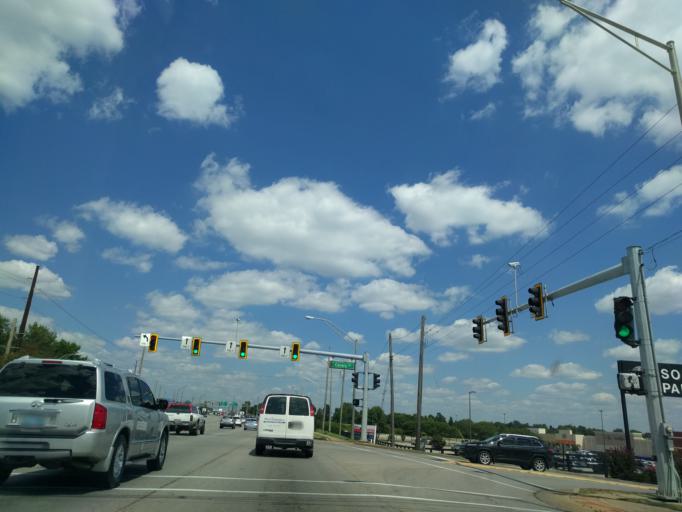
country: US
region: Kentucky
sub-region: Fayette County
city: Monticello
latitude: 37.9926
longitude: -84.5232
